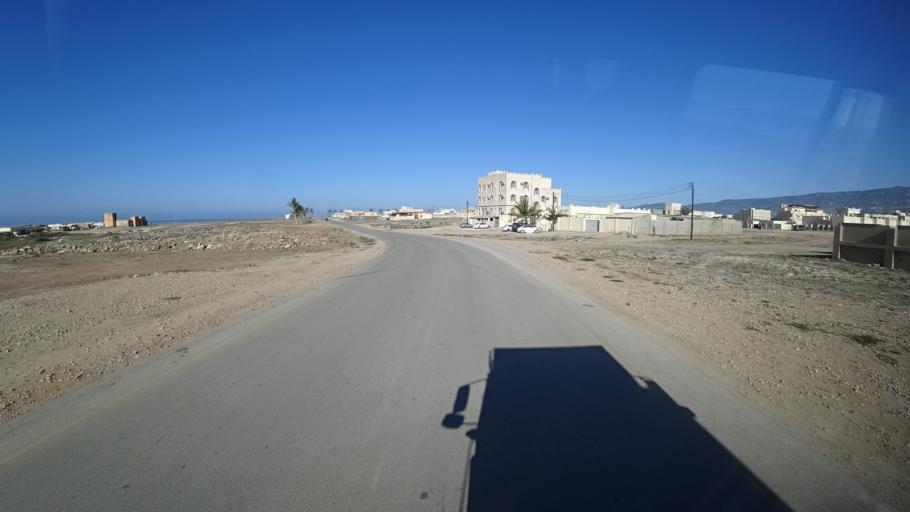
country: OM
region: Zufar
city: Salalah
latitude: 16.9777
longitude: 54.6950
